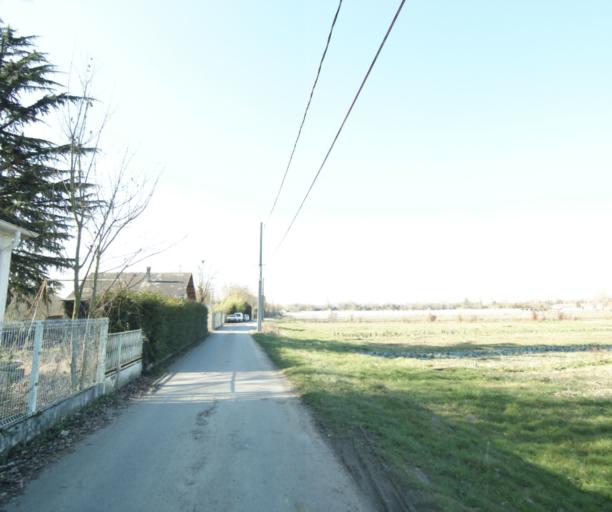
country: FR
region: Ile-de-France
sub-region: Departement du Val-d'Oise
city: Neuville-sur-Oise
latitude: 49.0228
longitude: 2.0686
